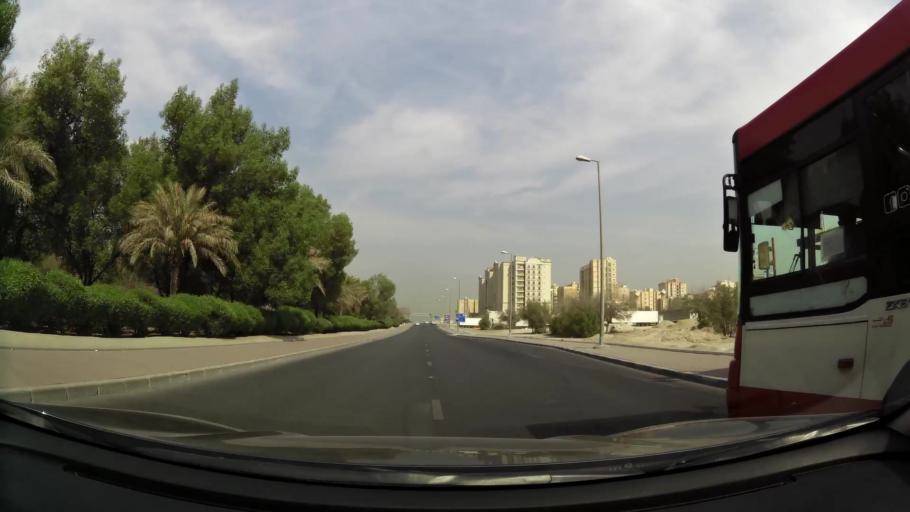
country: KW
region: Al Farwaniyah
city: Janub as Surrah
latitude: 29.2734
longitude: 47.9699
